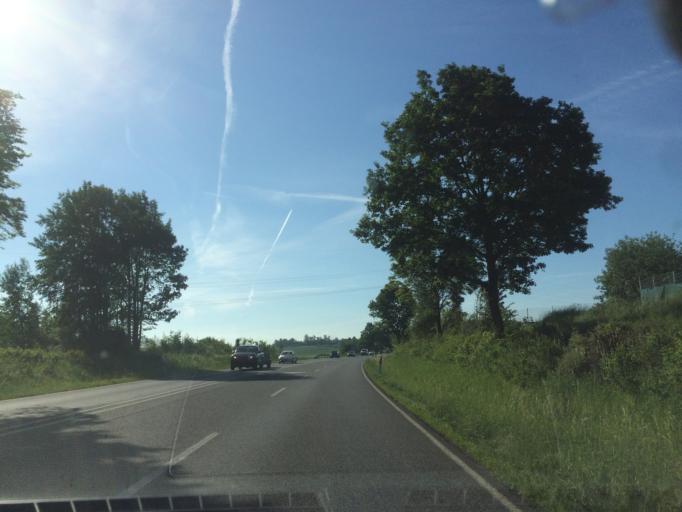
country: DE
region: Hesse
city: Grebenstein
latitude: 51.4362
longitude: 9.4173
